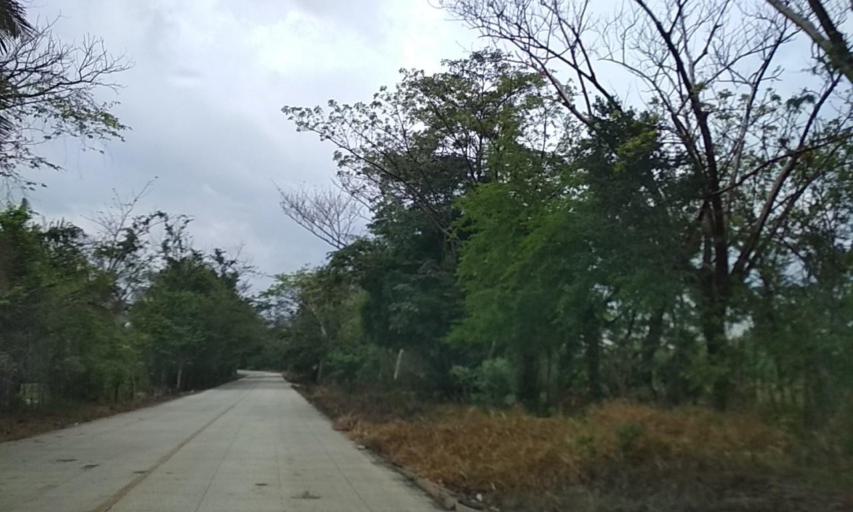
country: MX
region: Tabasco
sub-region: Huimanguillo
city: Francisco Rueda
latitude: 17.6664
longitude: -94.0908
